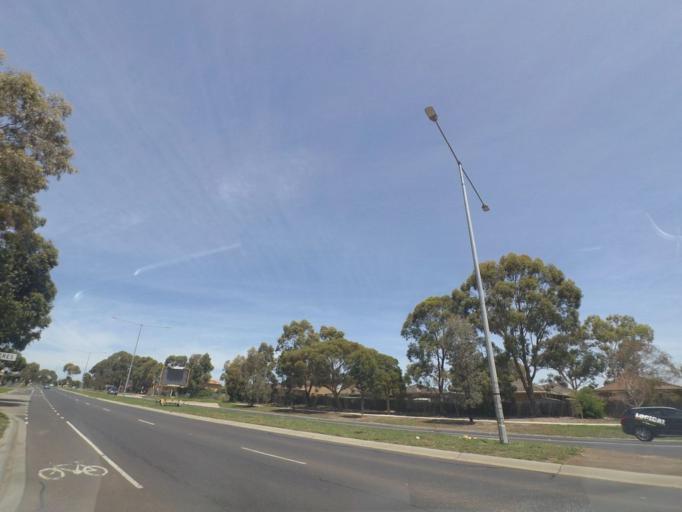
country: AU
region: Victoria
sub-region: Brimbank
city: Keilor Downs
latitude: -37.7257
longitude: 144.8116
